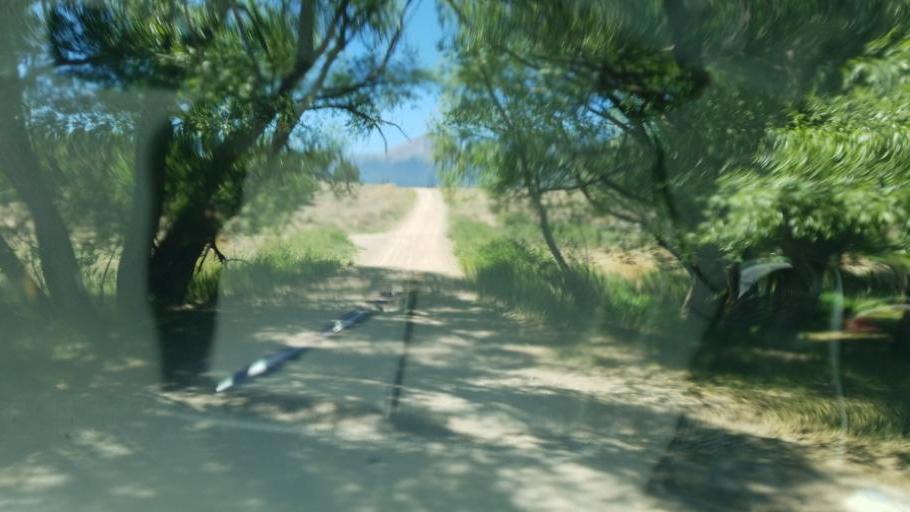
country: US
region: Colorado
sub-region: Custer County
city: Westcliffe
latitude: 38.3030
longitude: -105.6150
